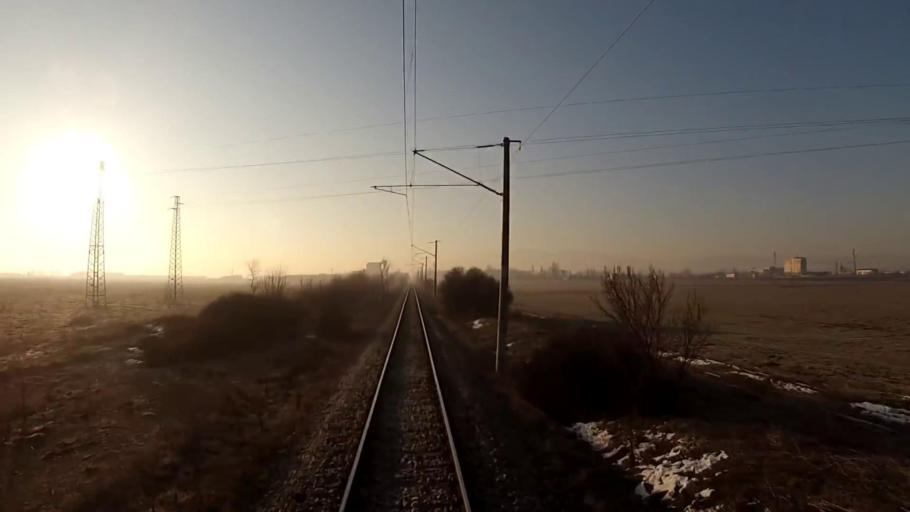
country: BG
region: Sofiya
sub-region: Obshtina Kostinbrod
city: Kostinbrod
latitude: 42.7942
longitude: 23.2085
